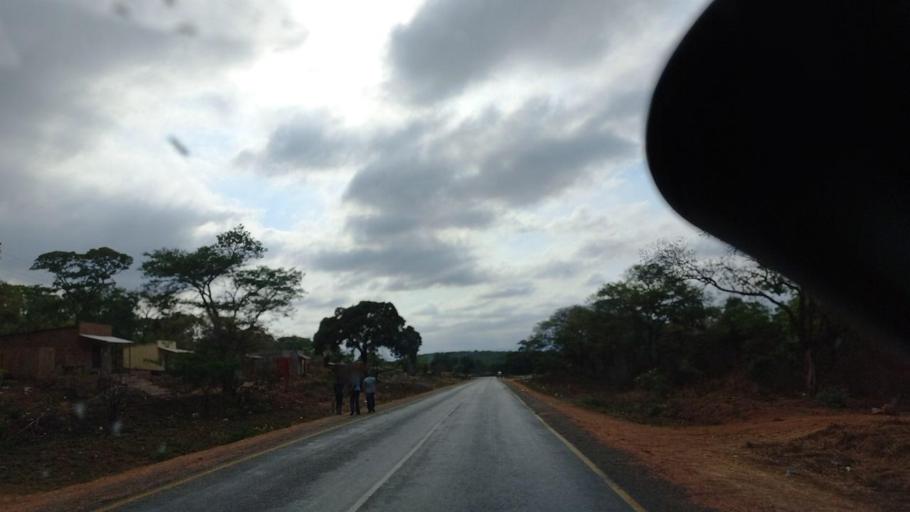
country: ZM
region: Lusaka
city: Chongwe
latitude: -15.2710
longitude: 28.9011
